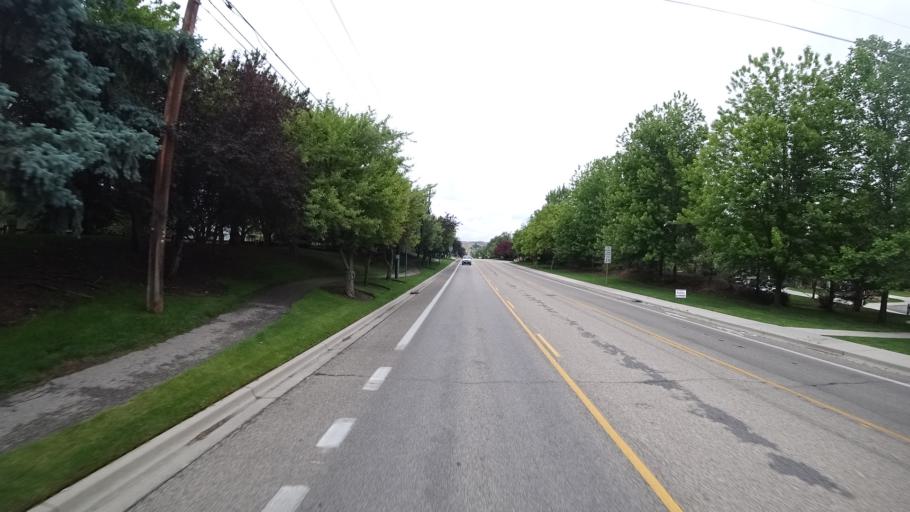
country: US
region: Idaho
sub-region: Ada County
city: Eagle
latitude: 43.7065
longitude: -116.3238
